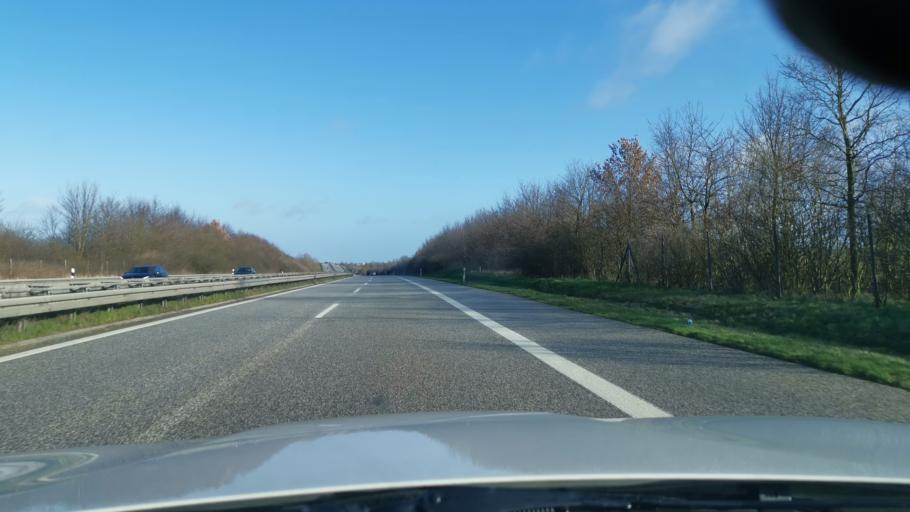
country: DE
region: Mecklenburg-Vorpommern
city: Kritzmow
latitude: 54.0651
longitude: 12.0484
